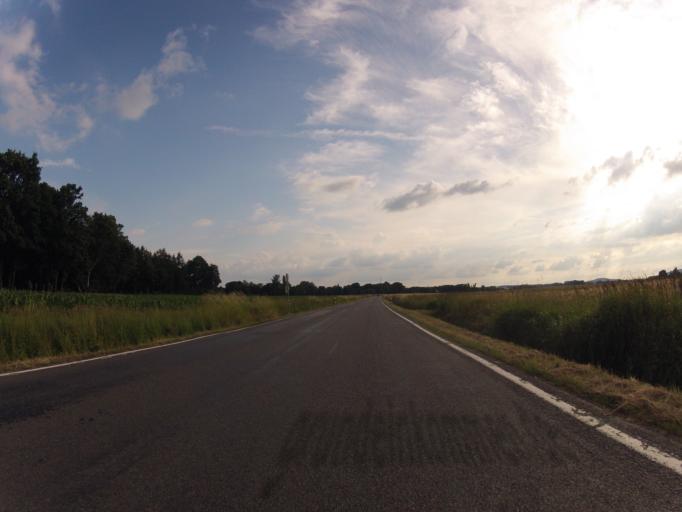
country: DE
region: Saxony
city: Falkenhain
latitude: 51.4132
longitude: 12.8919
